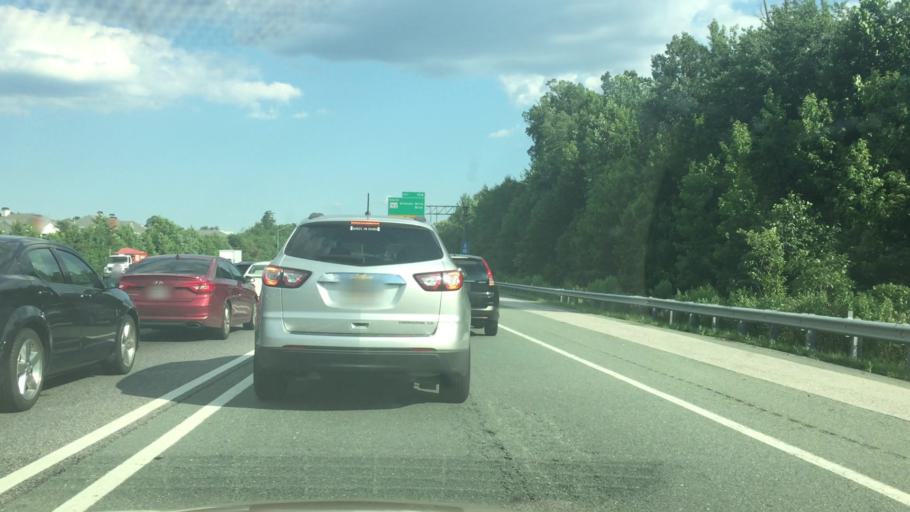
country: US
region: Maryland
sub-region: Howard County
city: Hanover
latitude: 39.1653
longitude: -76.7248
